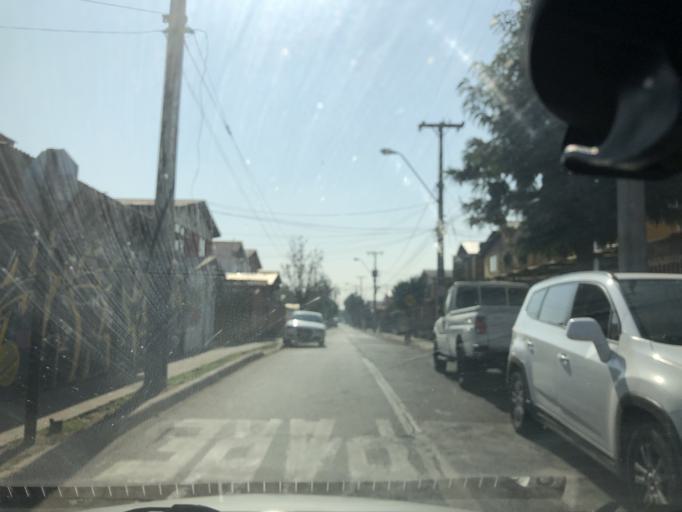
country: CL
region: Santiago Metropolitan
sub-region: Provincia de Cordillera
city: Puente Alto
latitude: -33.5934
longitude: -70.5694
